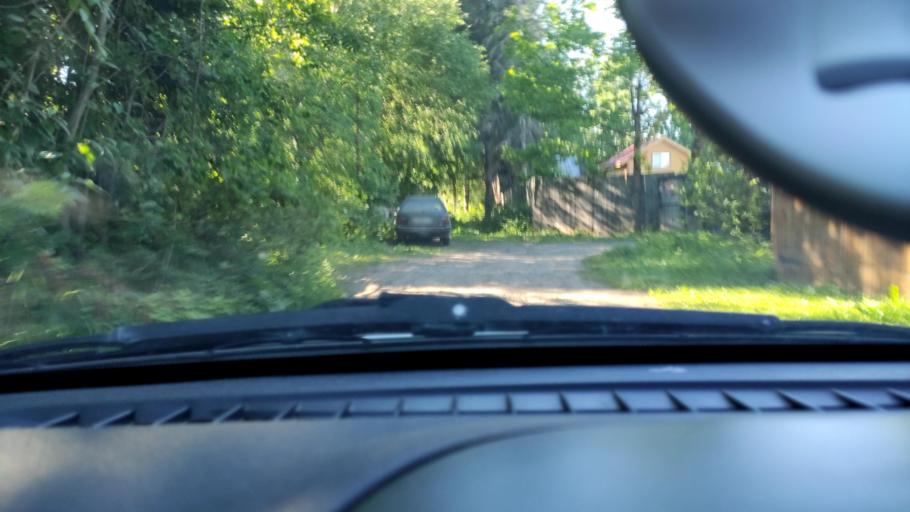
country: RU
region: Perm
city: Bershet'
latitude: 57.7001
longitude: 56.4069
